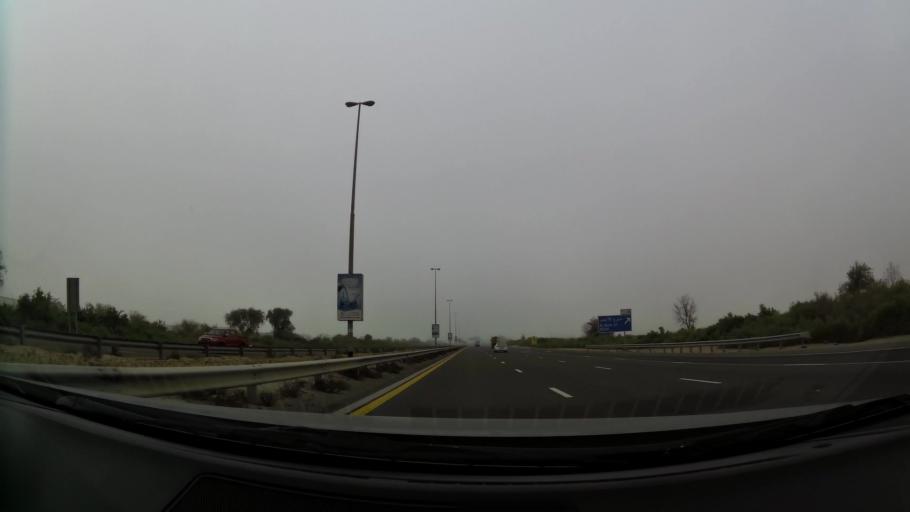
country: AE
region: Dubai
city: Dubai
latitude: 25.1361
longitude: 55.3511
